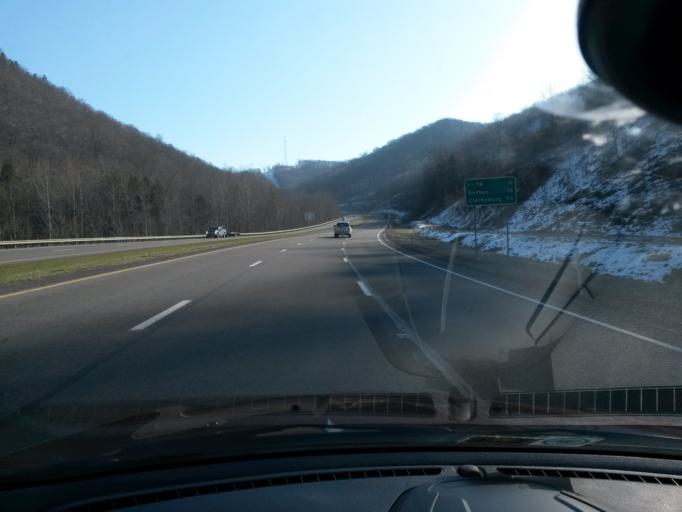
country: US
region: West Virginia
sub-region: Braxton County
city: Sutton
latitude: 38.5109
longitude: -80.7422
